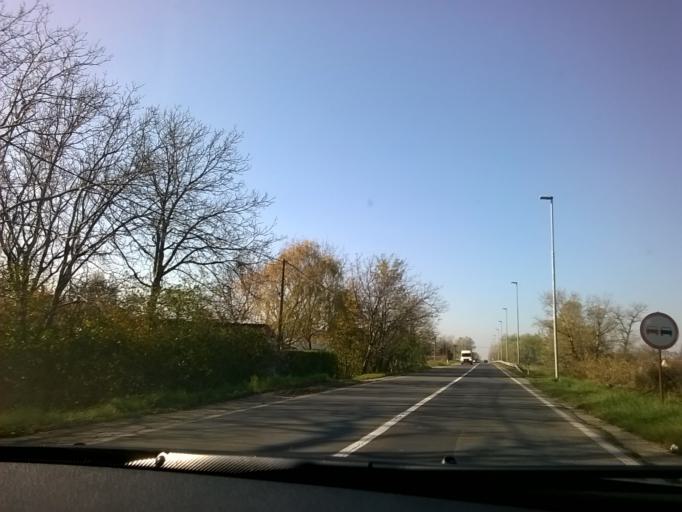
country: RS
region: Autonomna Pokrajina Vojvodina
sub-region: Juznobanatski Okrug
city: Pancevo
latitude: 44.8659
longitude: 20.5878
